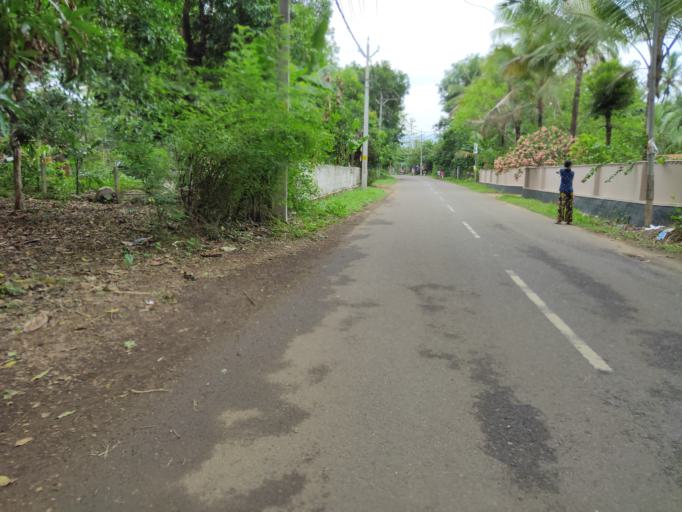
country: IN
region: Kerala
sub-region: Malappuram
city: Manjeri
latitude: 11.2651
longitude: 76.2357
